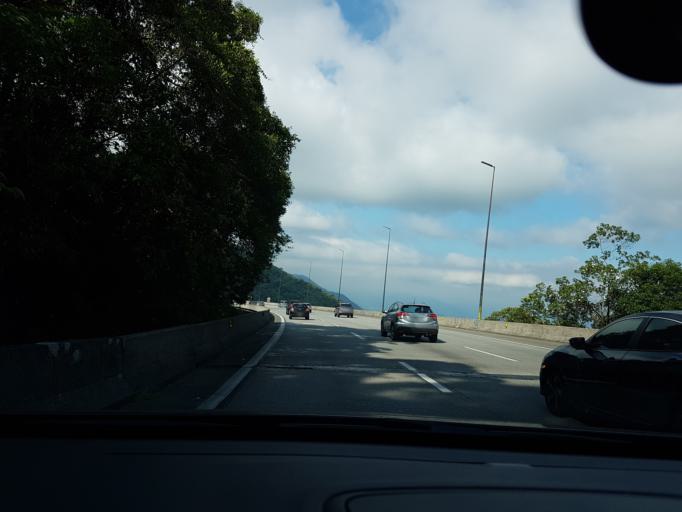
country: BR
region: Sao Paulo
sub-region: Cubatao
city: Cubatao
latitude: -23.9240
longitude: -46.5336
